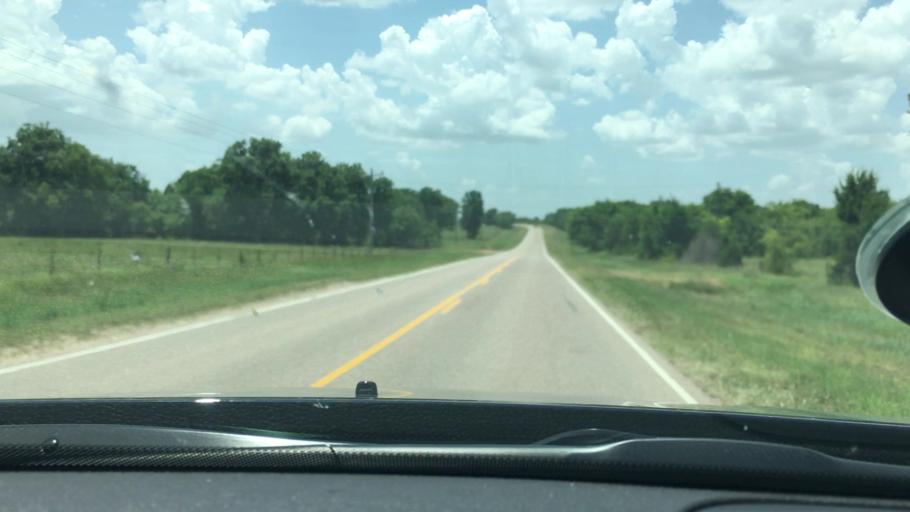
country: US
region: Oklahoma
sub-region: Johnston County
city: Tishomingo
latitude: 34.4772
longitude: -96.6317
